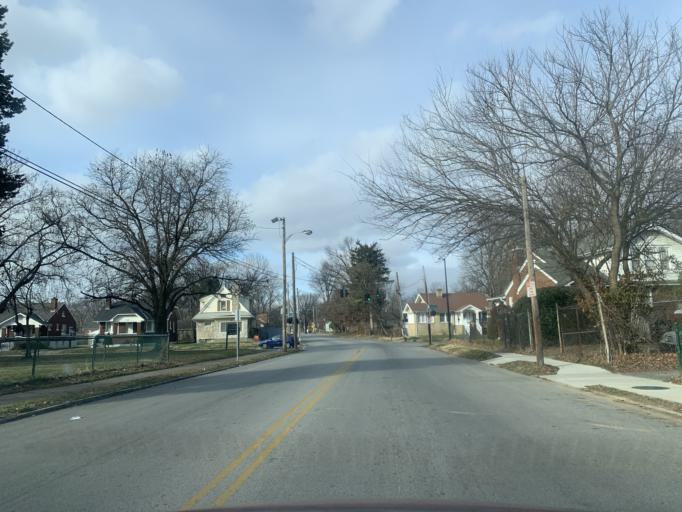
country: US
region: Kentucky
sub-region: Jefferson County
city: Shively
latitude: 38.2302
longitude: -85.7980
